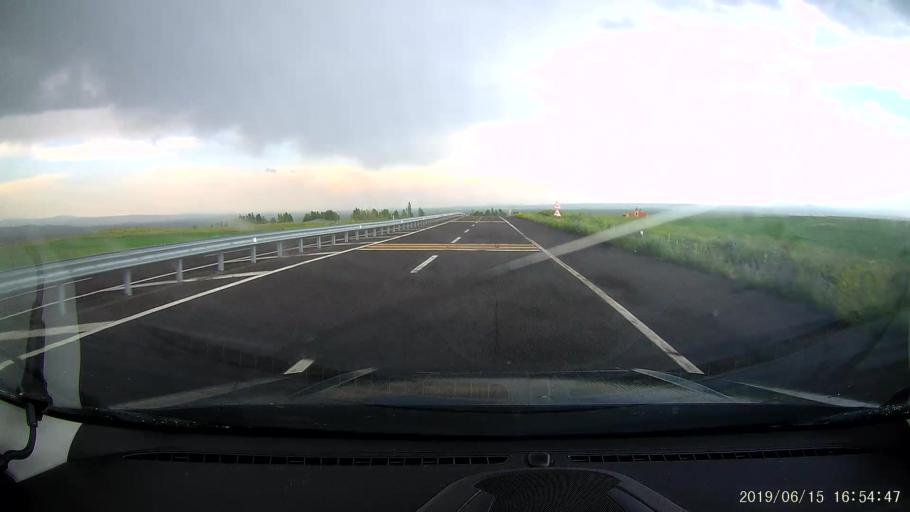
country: TR
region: Kars
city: Susuz
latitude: 40.7886
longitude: 43.1321
